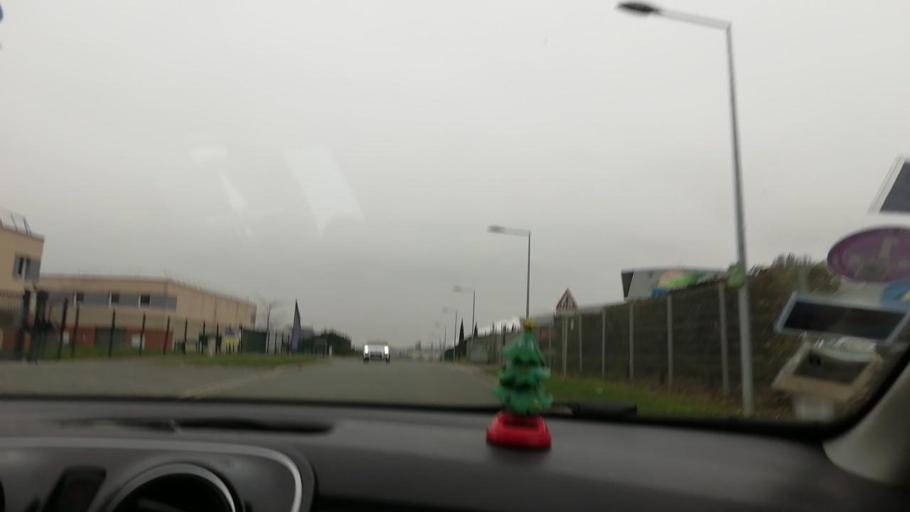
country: FR
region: Ile-de-France
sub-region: Departement de Seine-et-Marne
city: Saint-Soupplets
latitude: 49.0313
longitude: 2.7994
